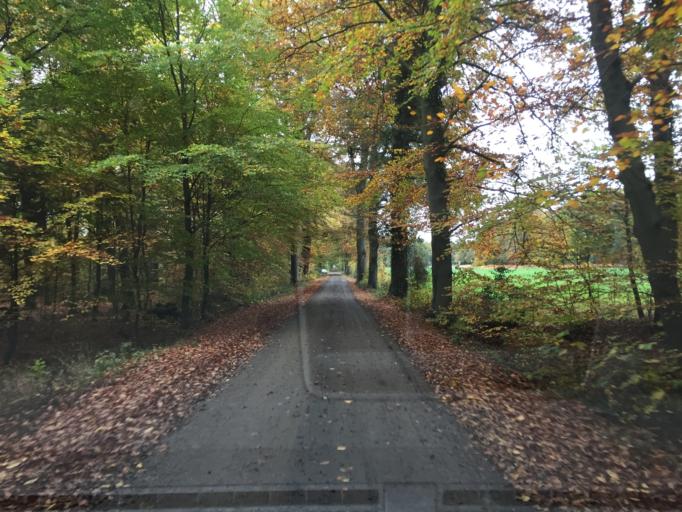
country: DE
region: Lower Saxony
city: Linsburg
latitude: 52.5777
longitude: 9.3158
